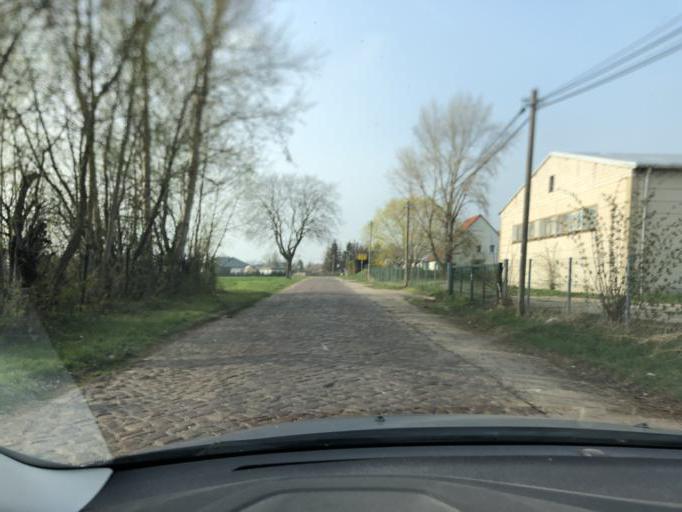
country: DE
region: Saxony-Anhalt
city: Zorbig
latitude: 51.5996
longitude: 12.1154
